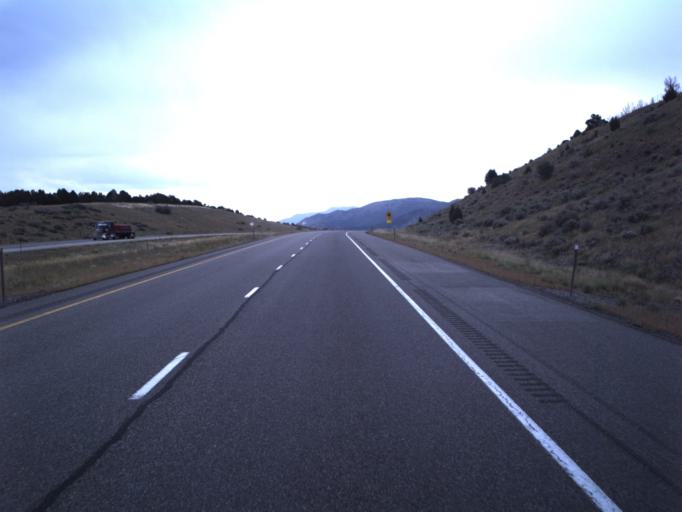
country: US
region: Utah
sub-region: Sevier County
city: Monroe
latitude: 38.5538
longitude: -112.4179
